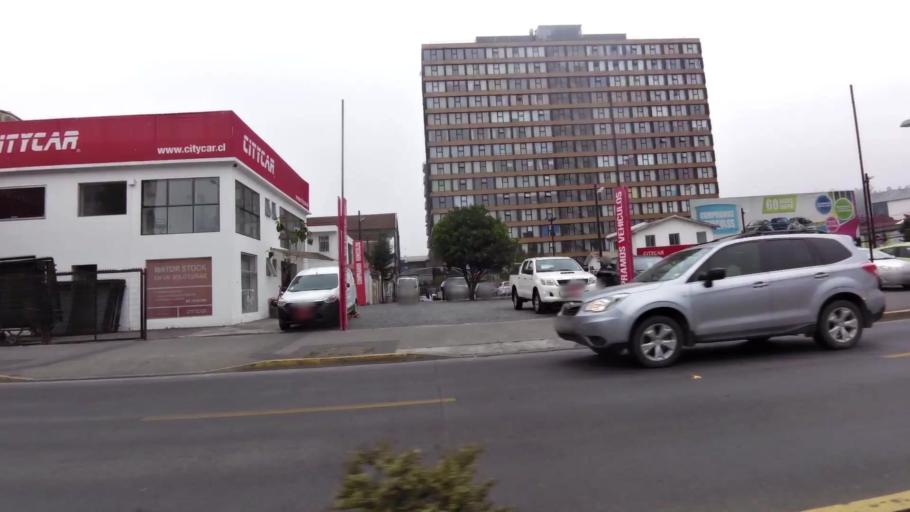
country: CL
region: Biobio
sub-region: Provincia de Concepcion
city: Concepcion
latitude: -36.8237
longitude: -73.0419
